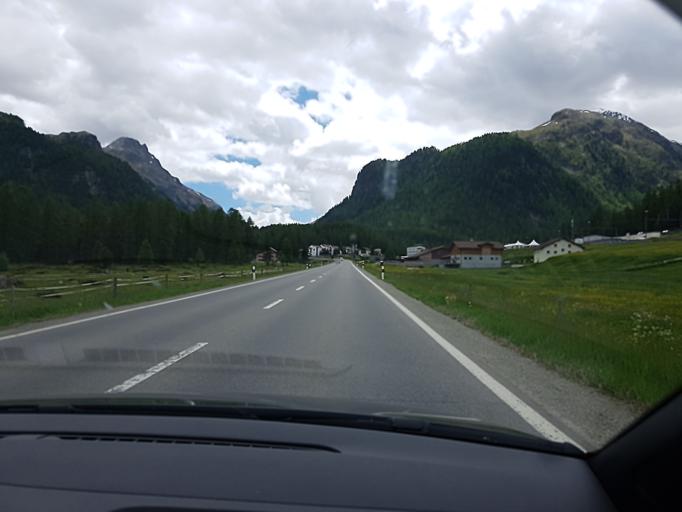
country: CH
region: Grisons
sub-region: Maloja District
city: Pontresina
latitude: 46.4951
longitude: 9.8937
